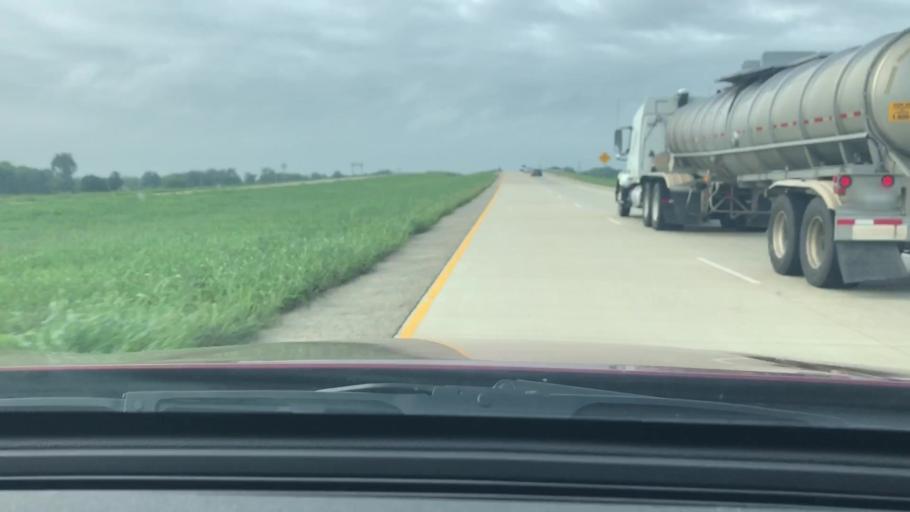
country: US
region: Louisiana
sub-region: Caddo Parish
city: Vivian
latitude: 32.8550
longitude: -93.8631
